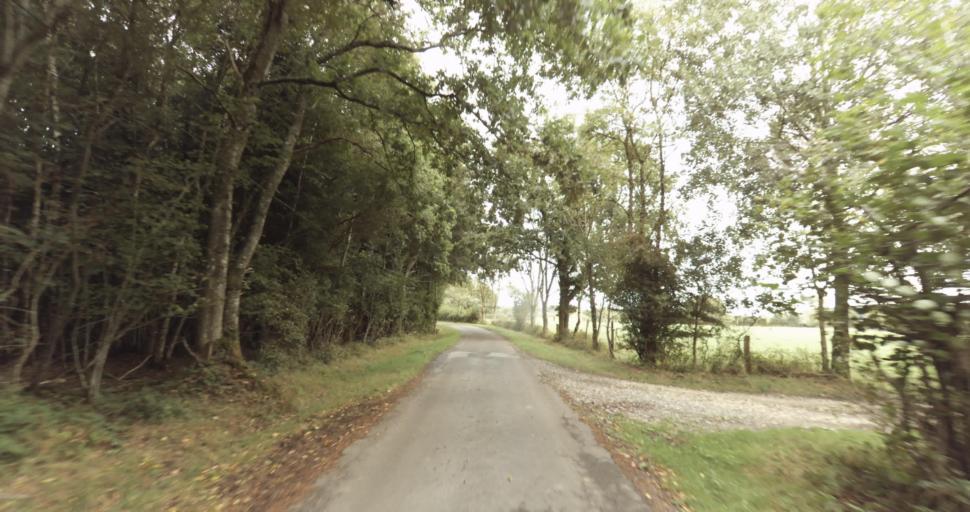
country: FR
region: Lower Normandy
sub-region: Departement de l'Orne
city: Gace
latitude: 48.7751
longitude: 0.3745
